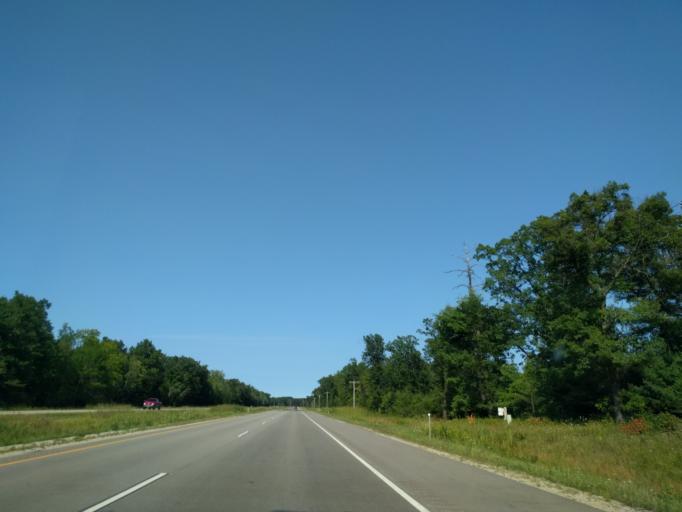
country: US
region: Wisconsin
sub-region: Oconto County
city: Oconto
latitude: 44.8442
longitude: -87.9083
